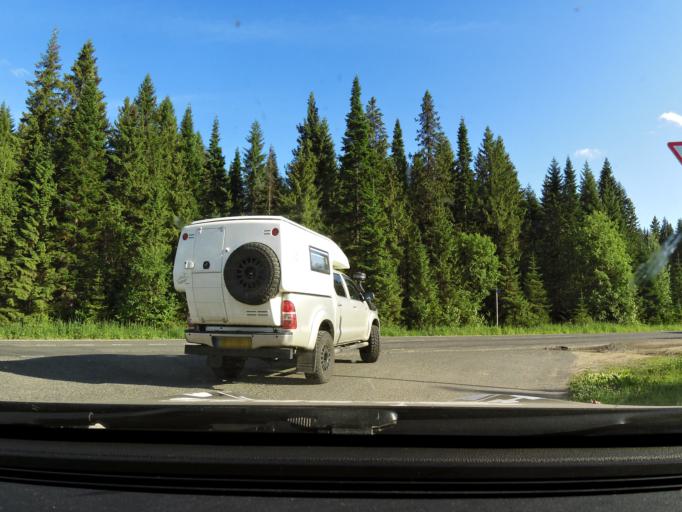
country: RU
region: Kirov
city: Omutninsk
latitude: 58.6854
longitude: 52.1481
